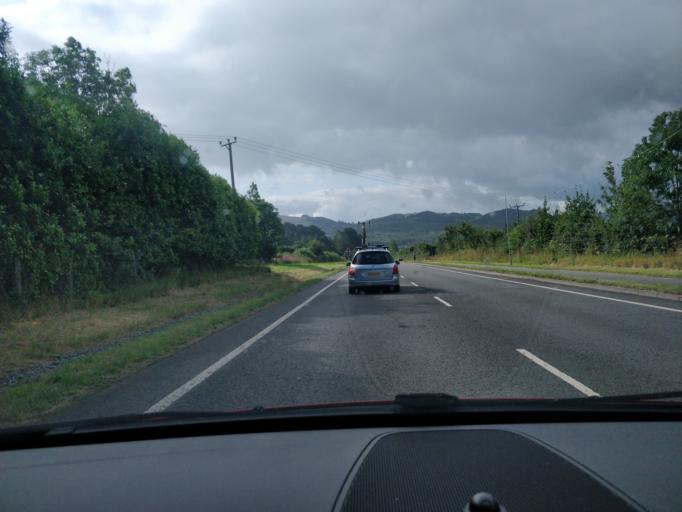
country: GB
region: Wales
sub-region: Conwy
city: Llanrwst
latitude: 53.1247
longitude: -3.7827
